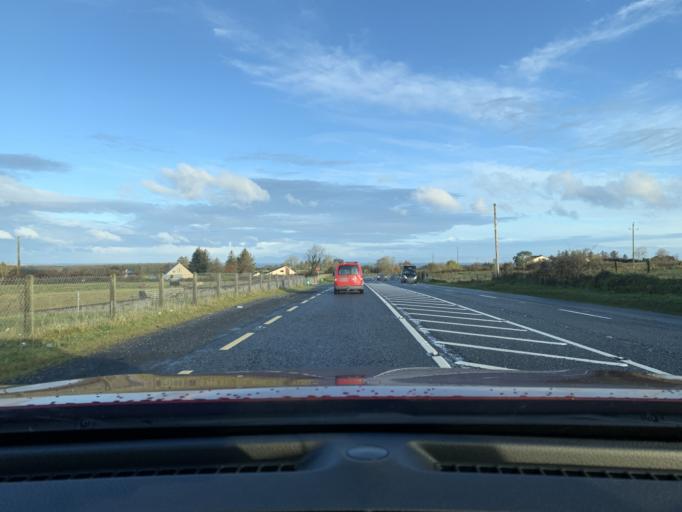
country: IE
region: Connaught
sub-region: Sligo
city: Strandhill
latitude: 54.3680
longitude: -8.5308
